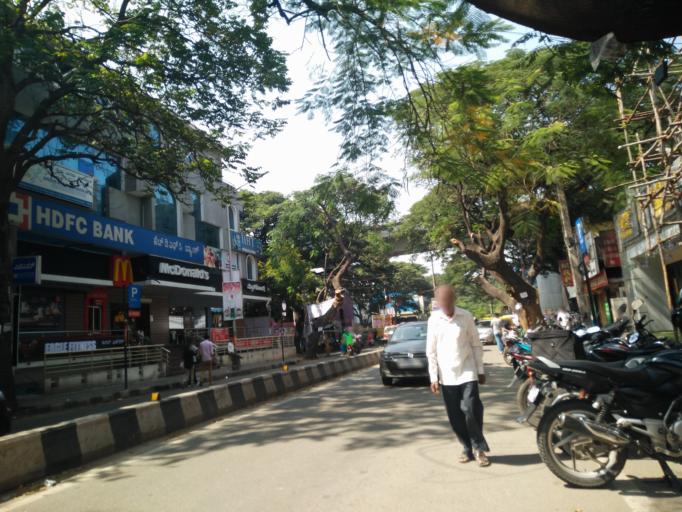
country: IN
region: Karnataka
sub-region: Bangalore Urban
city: Bangalore
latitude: 12.9686
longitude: 77.5373
